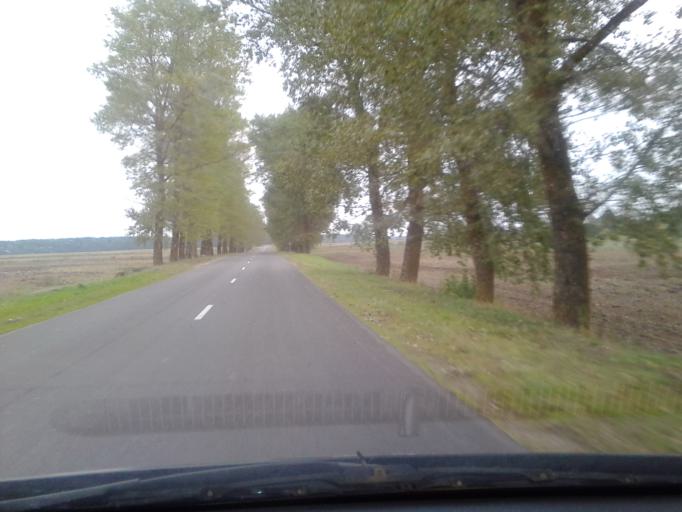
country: BY
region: Vitebsk
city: Pastavy
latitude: 55.1474
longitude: 26.9634
